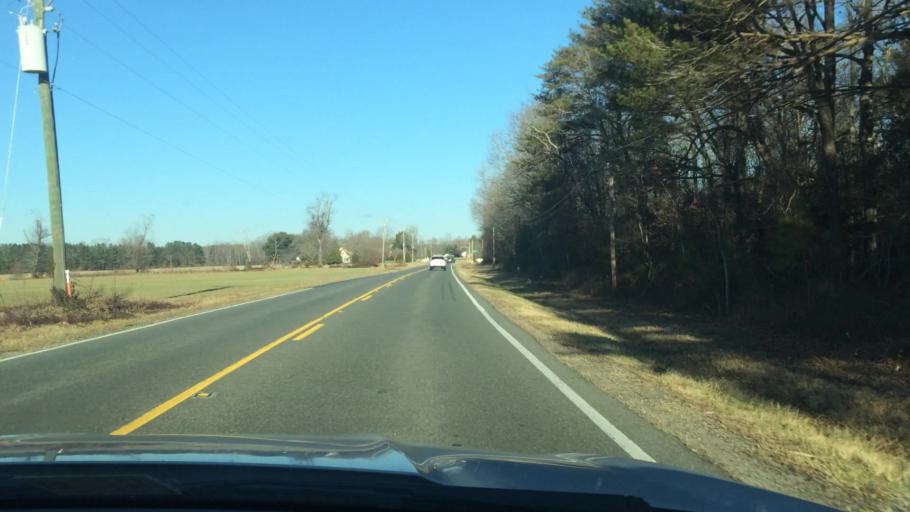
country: US
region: Virginia
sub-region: Lancaster County
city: Lancaster
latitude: 37.7558
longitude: -76.4165
